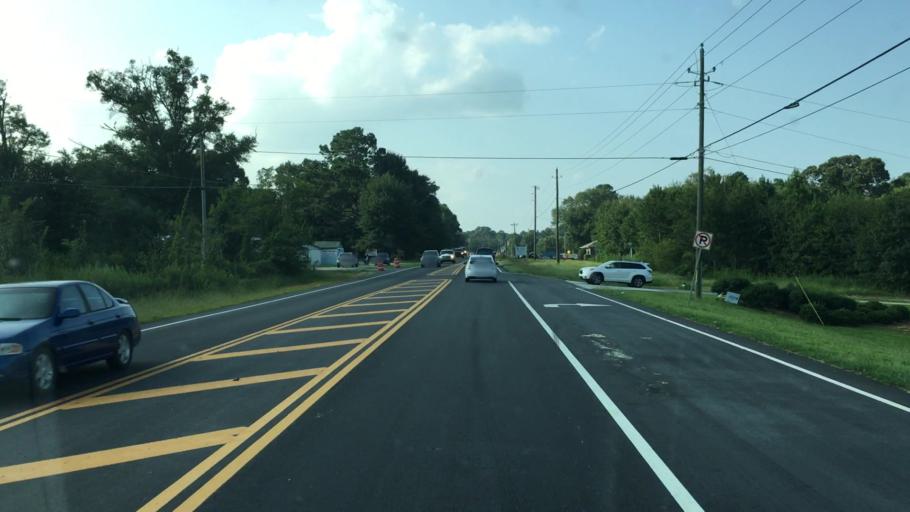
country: US
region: Georgia
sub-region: Jackson County
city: Braselton
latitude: 34.1259
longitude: -83.7648
